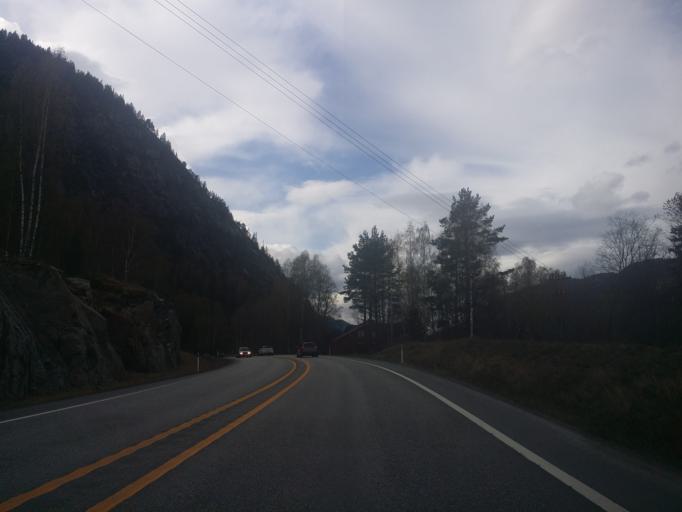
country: NO
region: Buskerud
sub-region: Nes
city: Nesbyen
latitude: 60.4600
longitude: 9.2590
